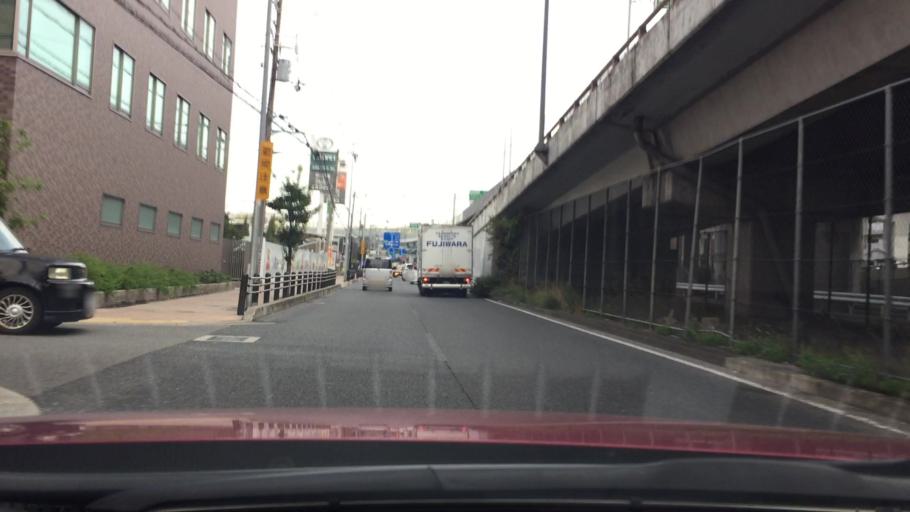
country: JP
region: Osaka
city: Kadoma
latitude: 34.7499
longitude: 135.5777
